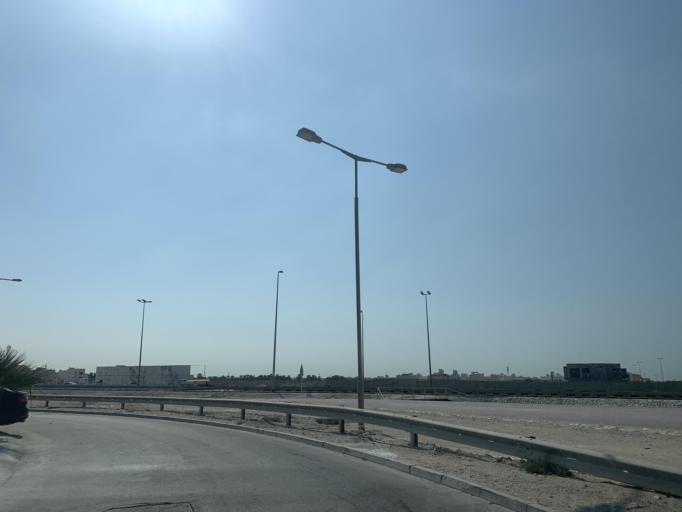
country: BH
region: Central Governorate
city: Madinat Hamad
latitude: 26.1136
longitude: 50.4939
